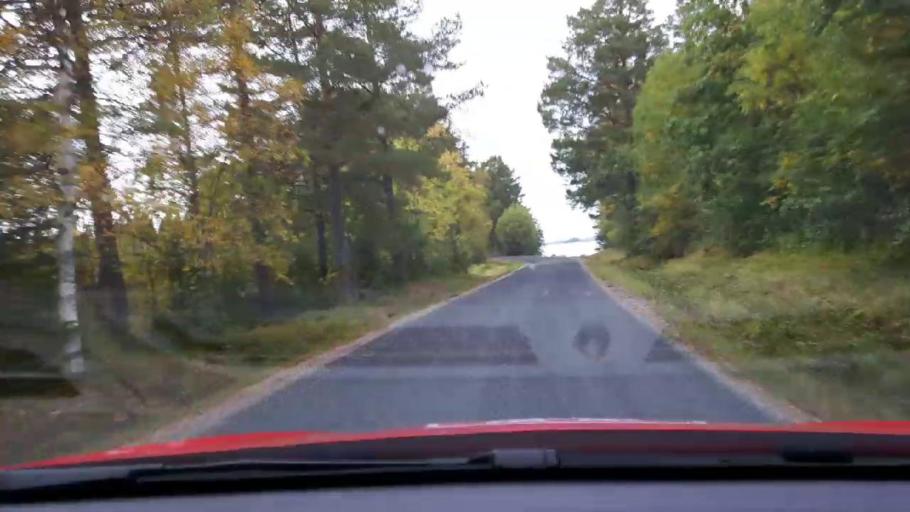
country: SE
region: Jaemtland
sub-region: Krokoms Kommun
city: Krokom
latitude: 63.1587
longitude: 14.1679
